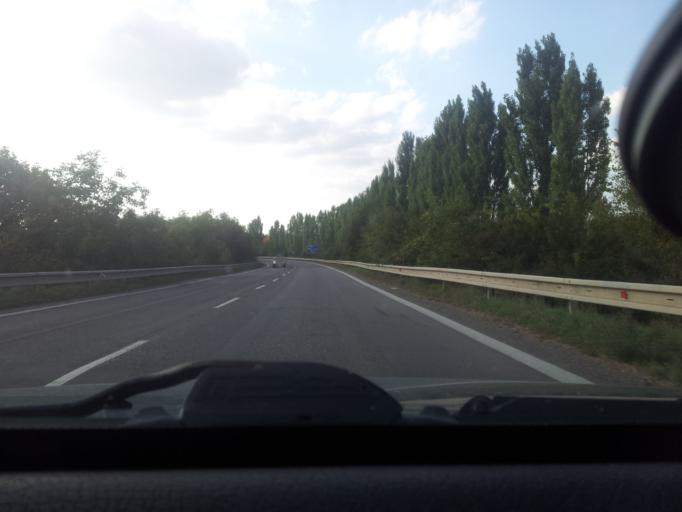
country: SK
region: Nitriansky
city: Levice
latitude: 48.2274
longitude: 18.6088
